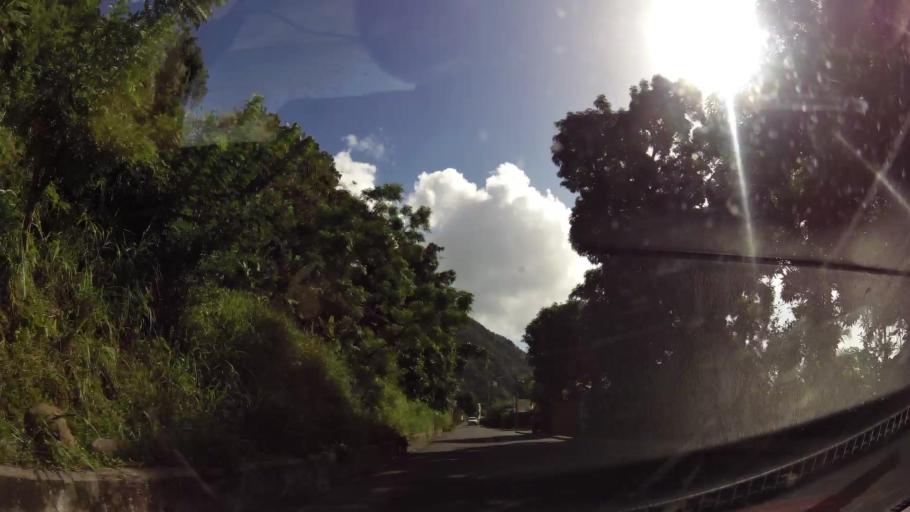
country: DM
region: Saint Luke
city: Pointe Michel
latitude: 15.2798
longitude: -61.3744
